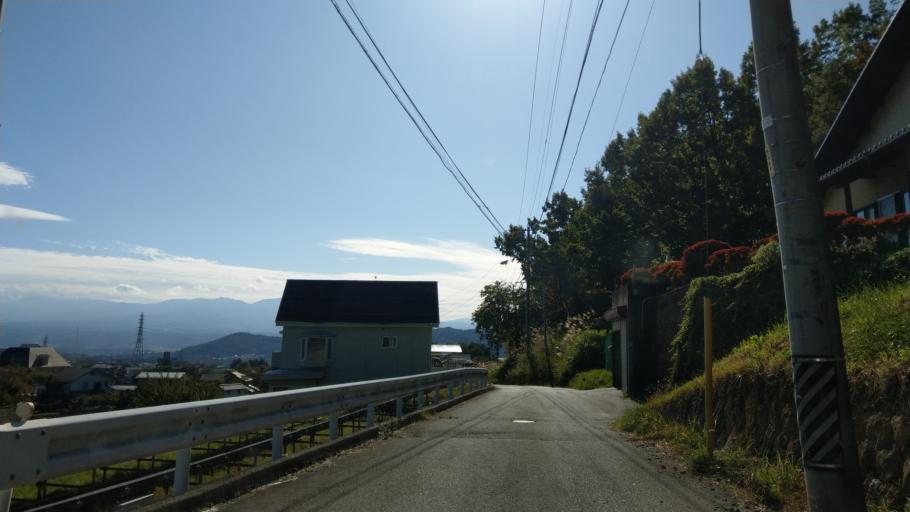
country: JP
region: Nagano
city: Komoro
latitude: 36.3369
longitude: 138.4365
